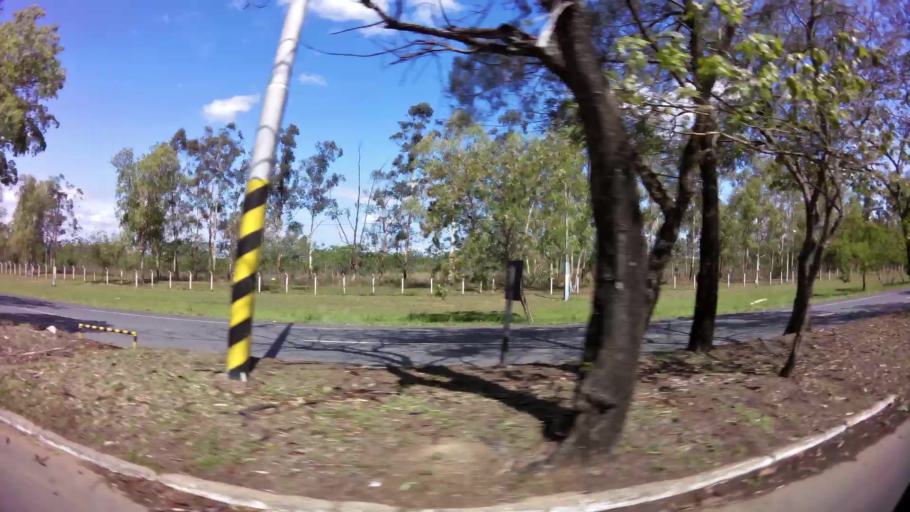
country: PY
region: Central
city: Fernando de la Mora
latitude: -25.2637
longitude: -57.5340
